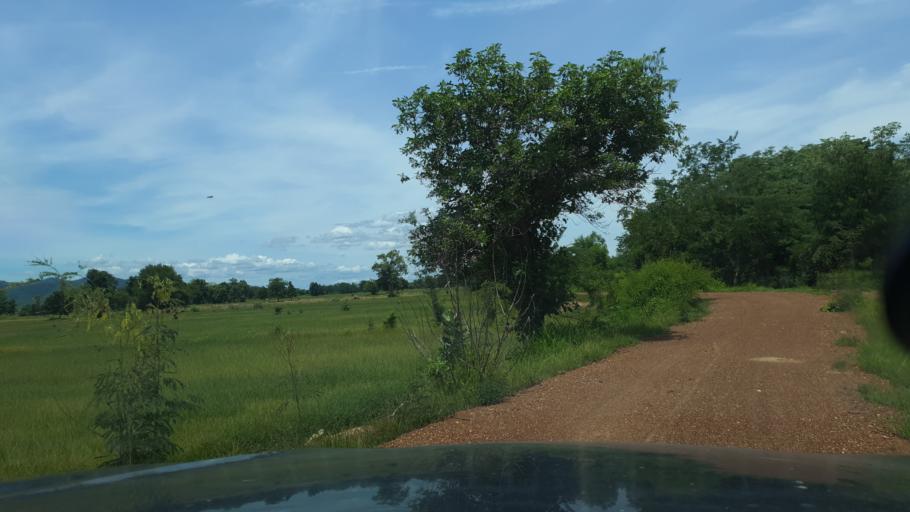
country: TH
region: Sukhothai
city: Ban Na
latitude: 17.0790
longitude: 99.6883
